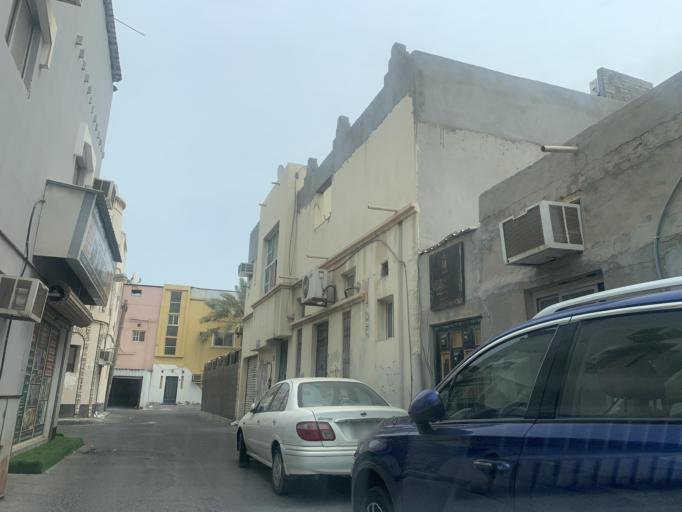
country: BH
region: Muharraq
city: Al Muharraq
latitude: 26.2802
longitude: 50.6343
